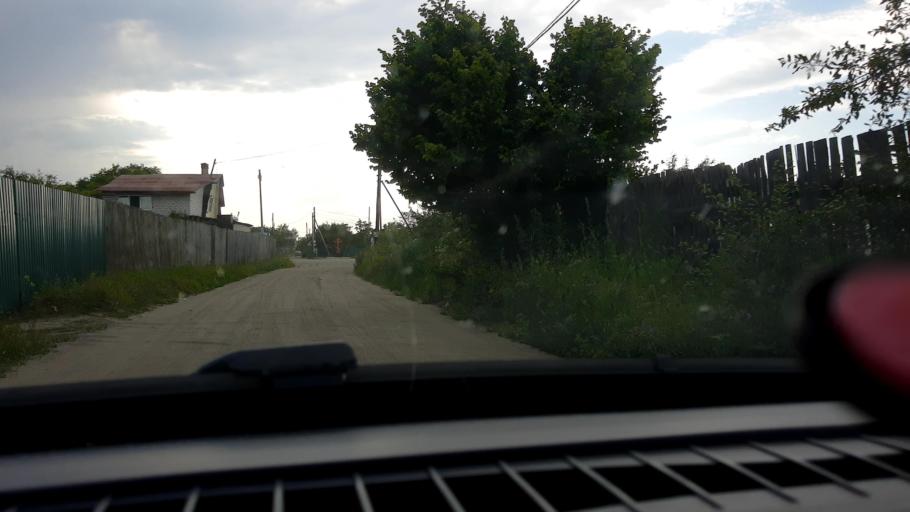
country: RU
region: Nizjnij Novgorod
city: Zavolzh'ye
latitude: 56.6590
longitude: 43.4259
